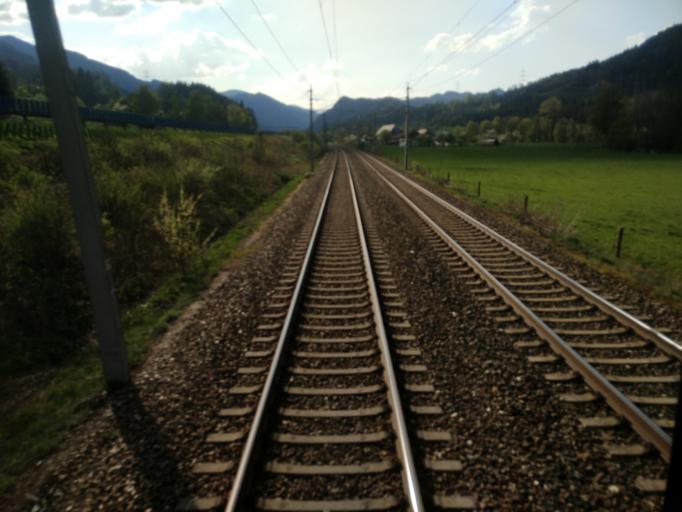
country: AT
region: Styria
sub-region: Politischer Bezirk Leoben
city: Mautern in Steiermark
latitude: 47.3941
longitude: 14.8607
